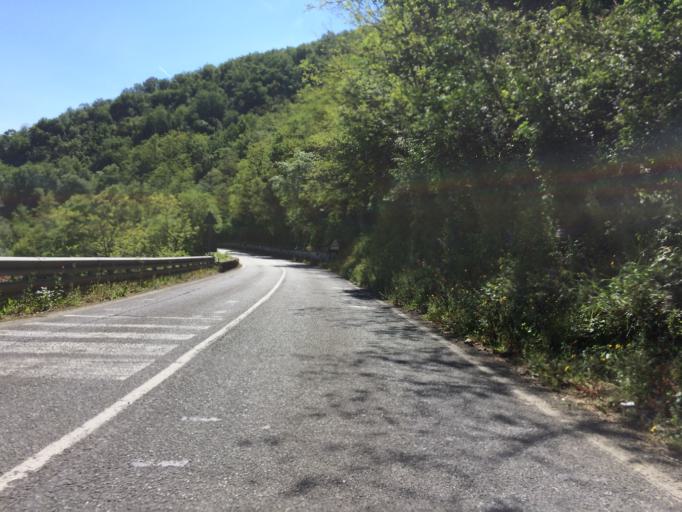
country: IT
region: Tuscany
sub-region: Provincia di Massa-Carrara
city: Montale
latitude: 44.1945
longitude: 9.9451
